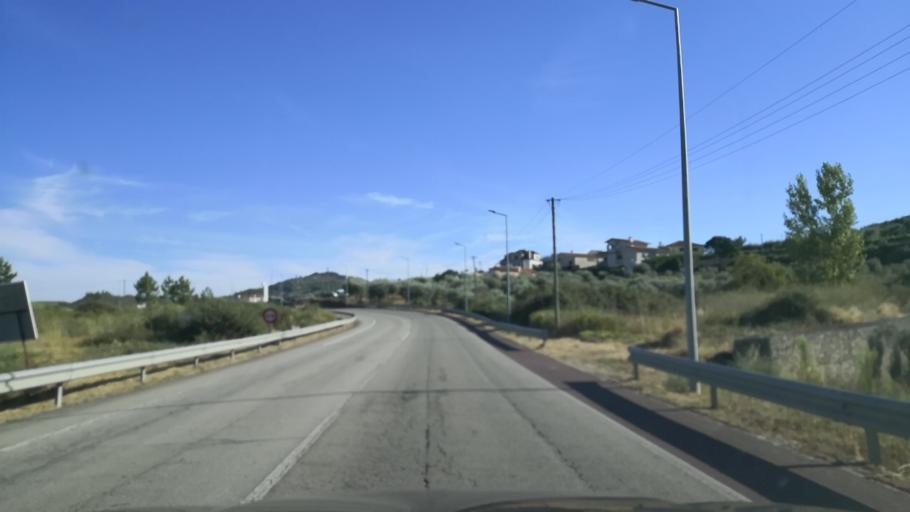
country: PT
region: Vila Real
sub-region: Murca
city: Murca
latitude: 41.4009
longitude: -7.4468
